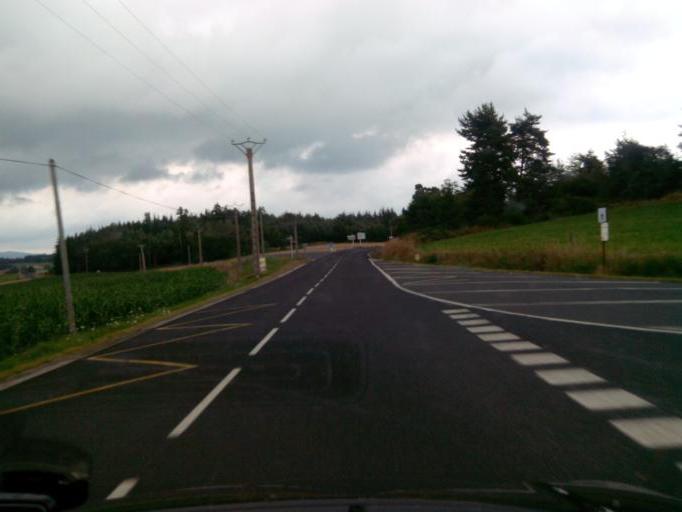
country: FR
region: Rhone-Alpes
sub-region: Departement de la Loire
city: Usson-en-Forez
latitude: 45.3546
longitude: 3.9905
